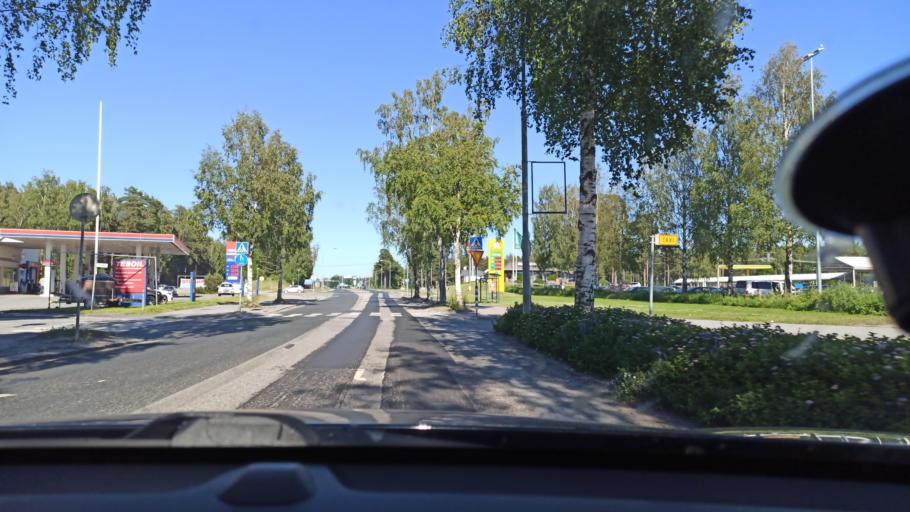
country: FI
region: Ostrobothnia
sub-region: Jakobstadsregionen
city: Jakobstad
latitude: 63.6781
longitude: 22.7170
